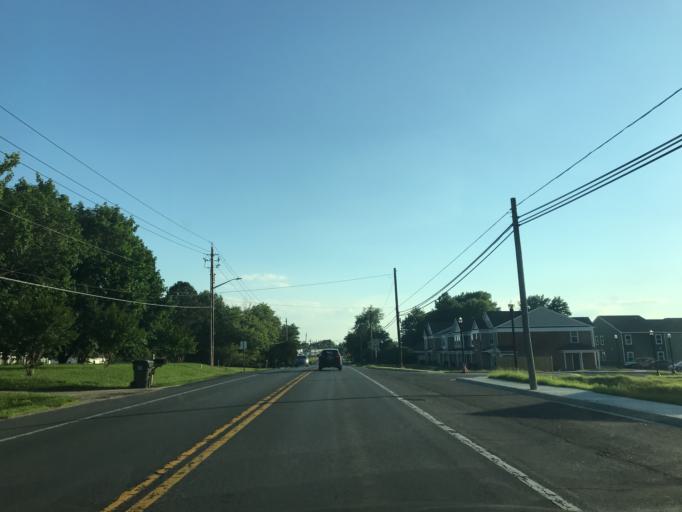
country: US
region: Maryland
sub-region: Talbot County
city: Easton
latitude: 38.7806
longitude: -76.0544
